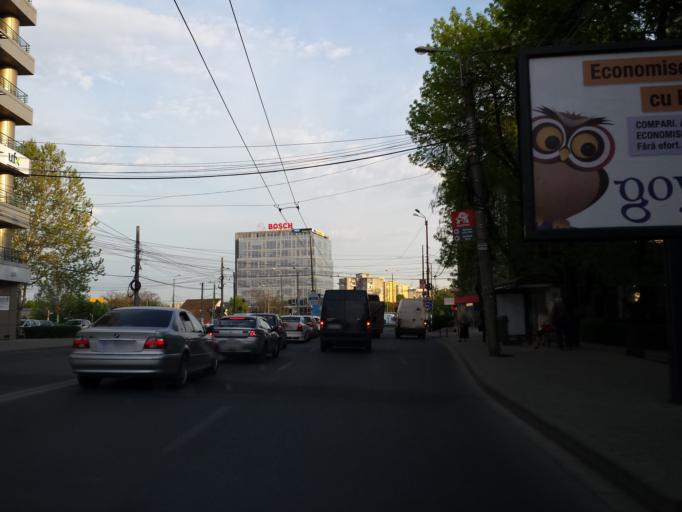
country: RO
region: Timis
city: Timisoara
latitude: 45.7651
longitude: 21.2242
